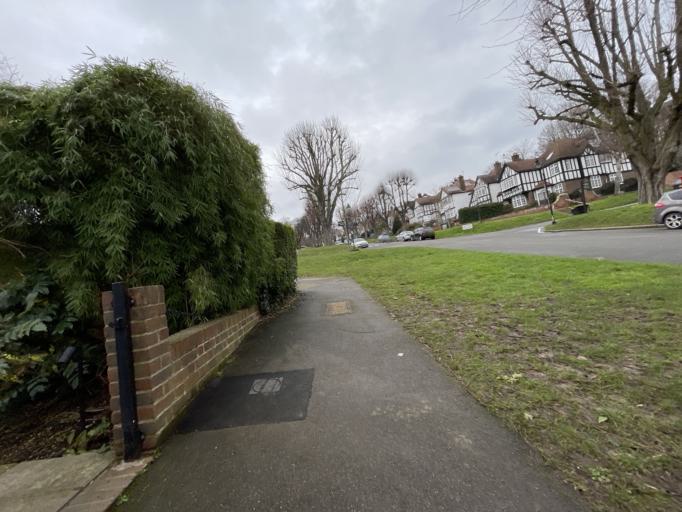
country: GB
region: England
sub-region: Greater London
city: Camden Town
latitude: 51.5645
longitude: -0.1494
